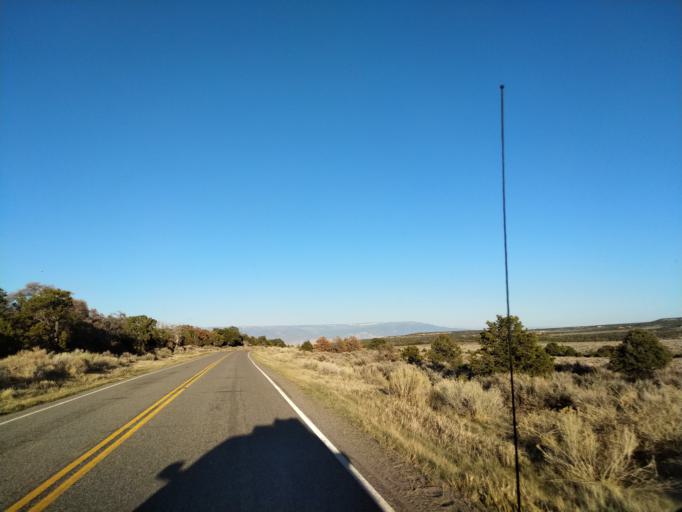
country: US
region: Colorado
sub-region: Mesa County
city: Redlands
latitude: 39.0050
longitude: -108.7031
